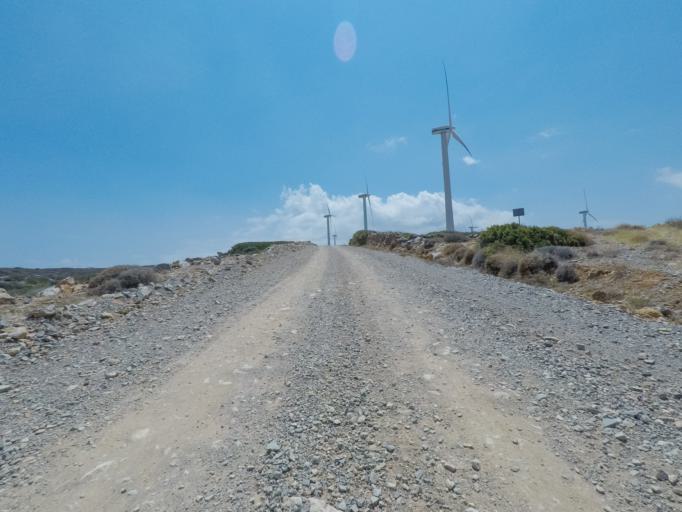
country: GR
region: Crete
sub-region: Nomos Lasithiou
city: Elounda
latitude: 35.3282
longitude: 25.7571
